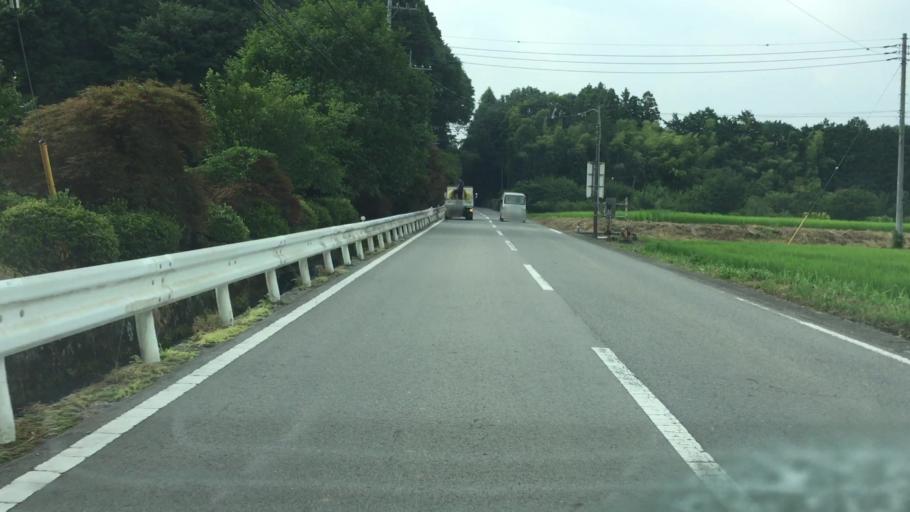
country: JP
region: Tochigi
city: Kuroiso
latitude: 36.9430
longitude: 139.9606
